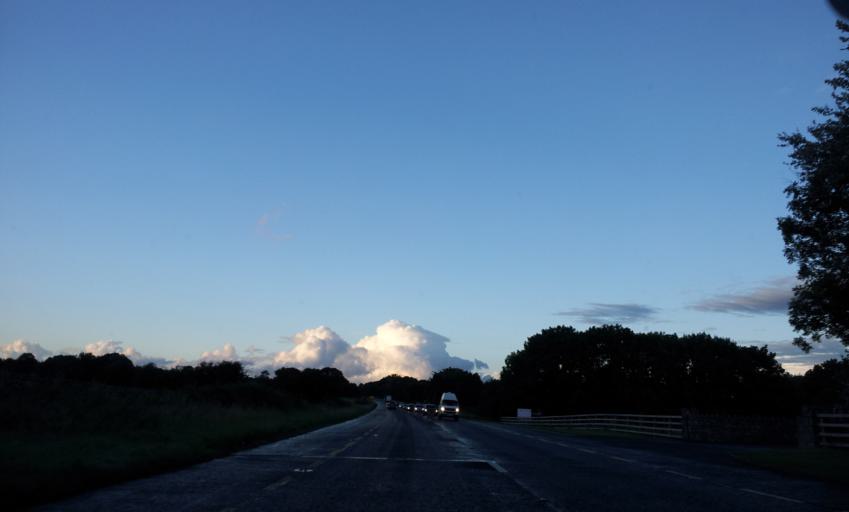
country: IE
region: Munster
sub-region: County Limerick
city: Rathkeale
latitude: 52.4990
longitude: -8.9941
